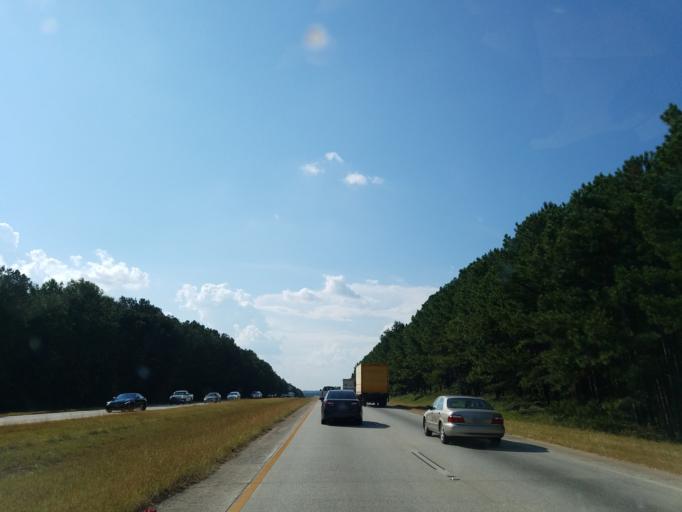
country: US
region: Georgia
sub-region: Barrow County
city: Auburn
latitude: 33.9637
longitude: -83.8016
